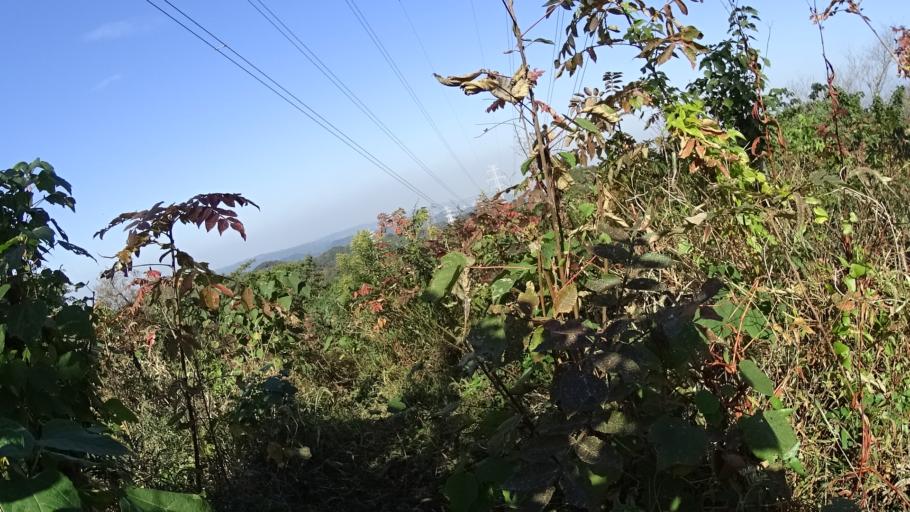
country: JP
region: Kanagawa
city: Yokosuka
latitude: 35.2752
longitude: 139.6230
